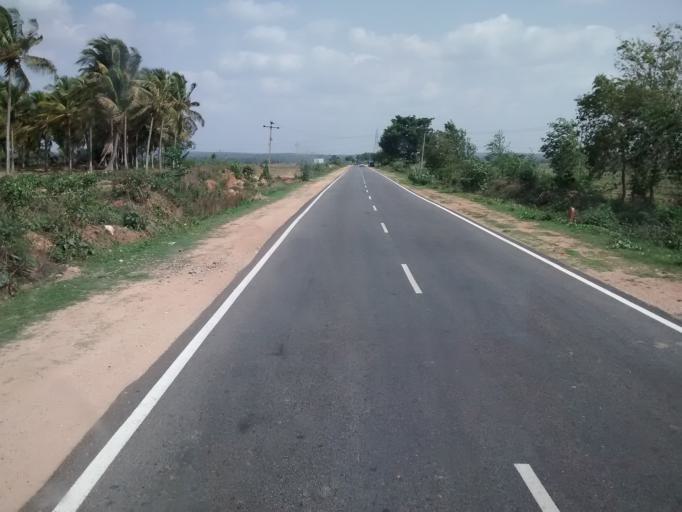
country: IN
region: Karnataka
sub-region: Mysore
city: Hunsur
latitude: 12.3879
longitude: 76.4096
